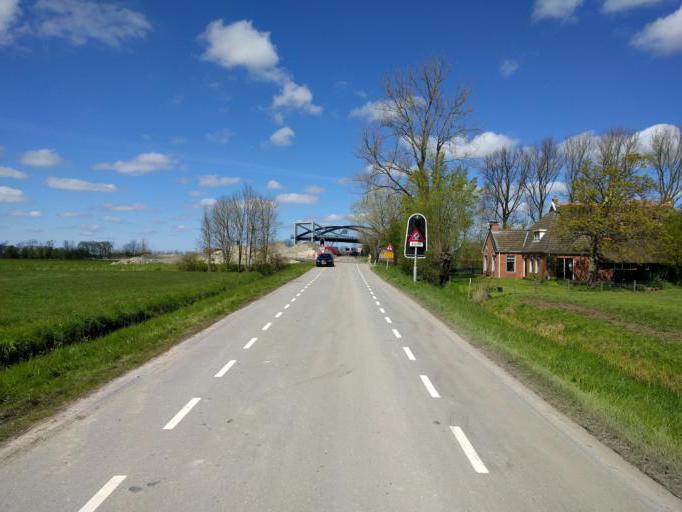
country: NL
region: Groningen
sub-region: Gemeente Zuidhorn
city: Aduard
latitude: 53.2570
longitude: 6.5028
